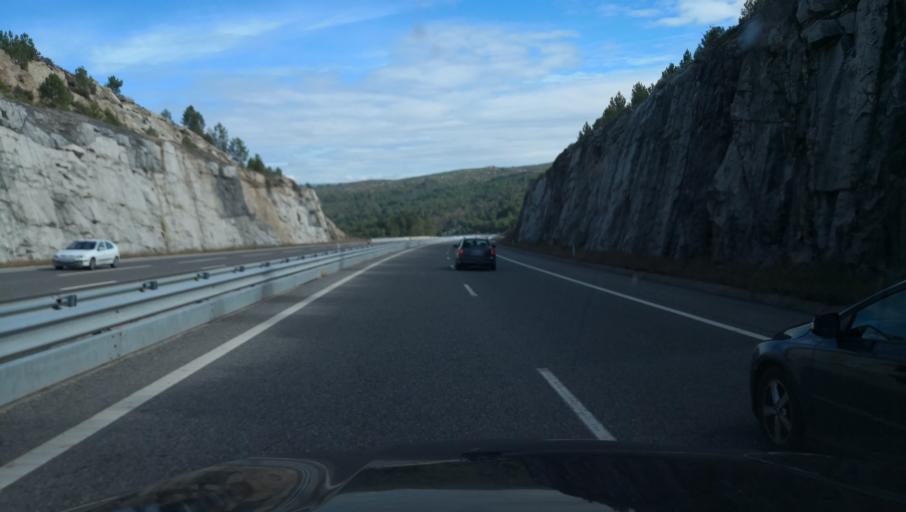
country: PT
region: Vila Real
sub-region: Boticas
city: Boticas
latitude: 41.6159
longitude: -7.6175
